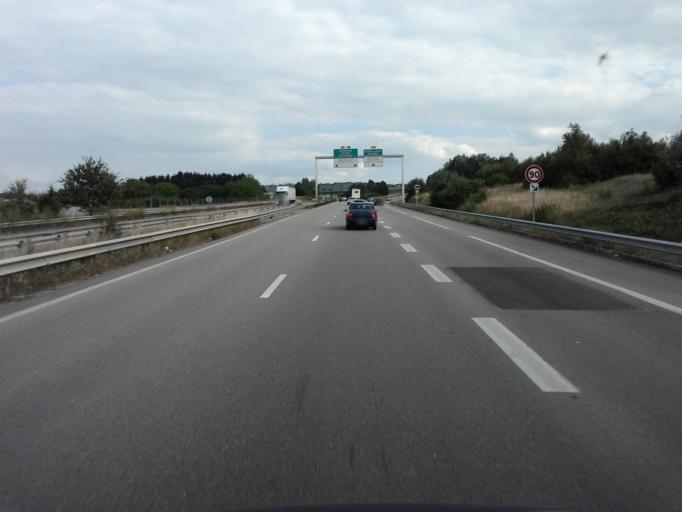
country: FR
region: Lorraine
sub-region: Departement des Vosges
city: Epinal
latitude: 48.1923
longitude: 6.4765
